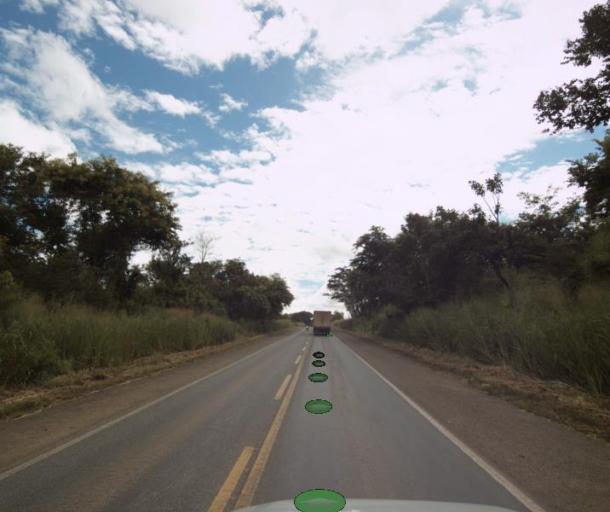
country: BR
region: Goias
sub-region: Uruacu
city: Uruacu
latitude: -14.4118
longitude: -49.1573
